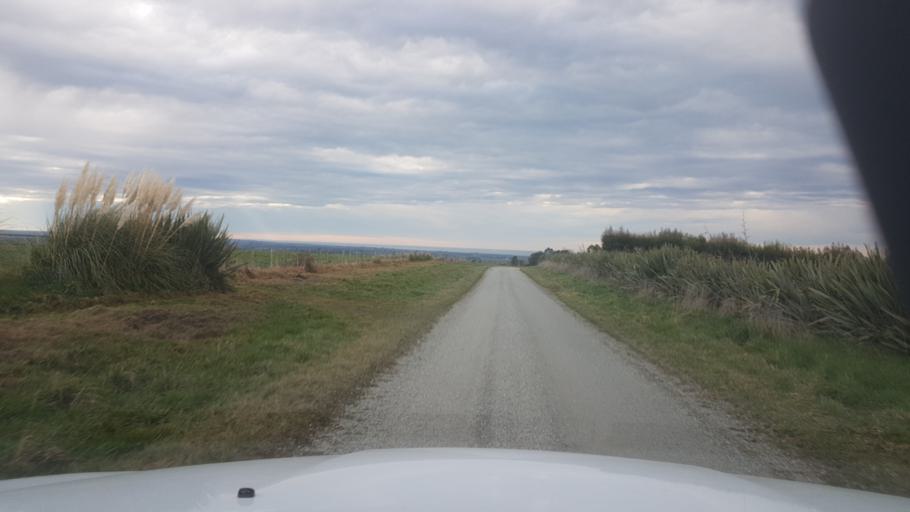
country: NZ
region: Canterbury
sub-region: Timaru District
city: Pleasant Point
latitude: -44.3457
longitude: 171.1241
